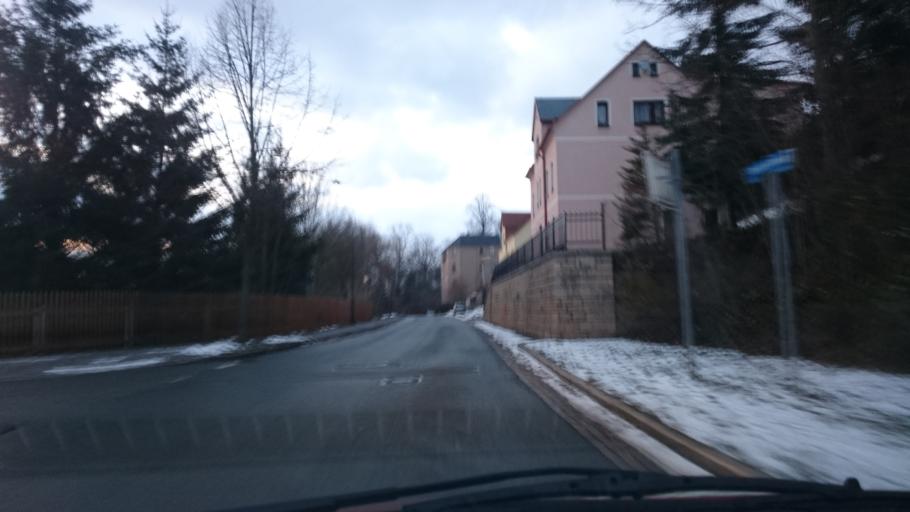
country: DE
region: Saxony
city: Wilkau-Hasslau
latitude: 50.7047
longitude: 12.5418
